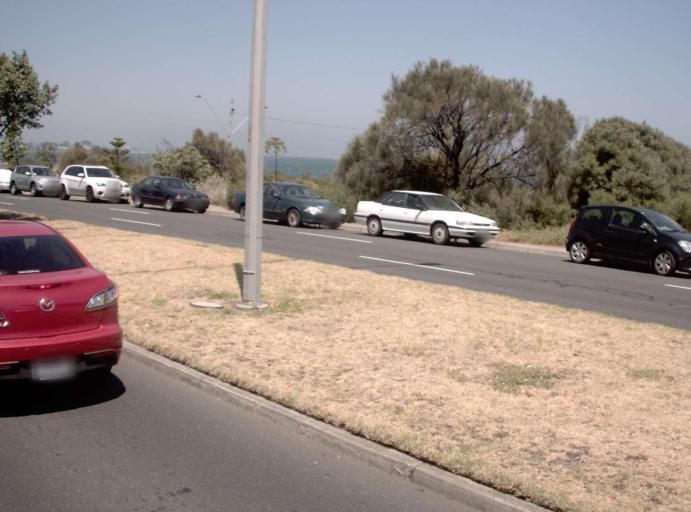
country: AU
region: Victoria
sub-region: Port Phillip
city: Elwood
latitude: -37.8839
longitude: 144.9794
